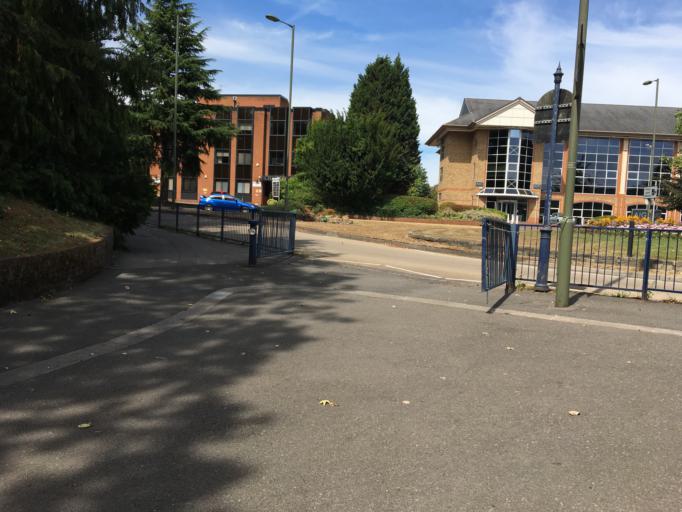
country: GB
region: England
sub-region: Surrey
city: Reigate
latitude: 51.2399
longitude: -0.2056
